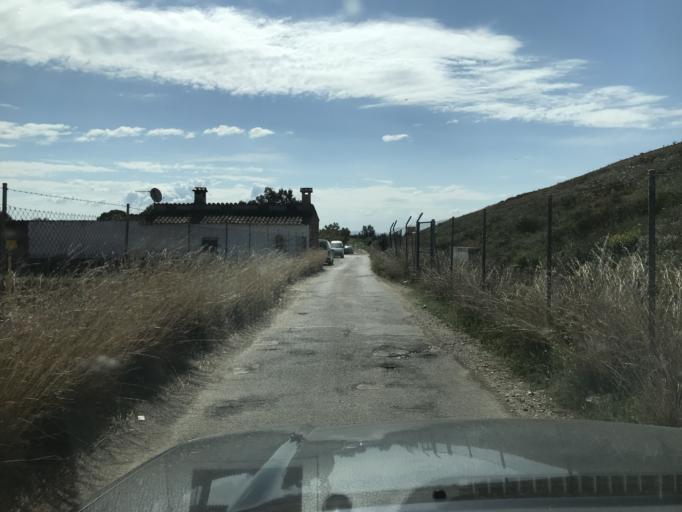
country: ES
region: Balearic Islands
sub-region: Illes Balears
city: Bunyola
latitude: 39.6460
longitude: 2.6871
